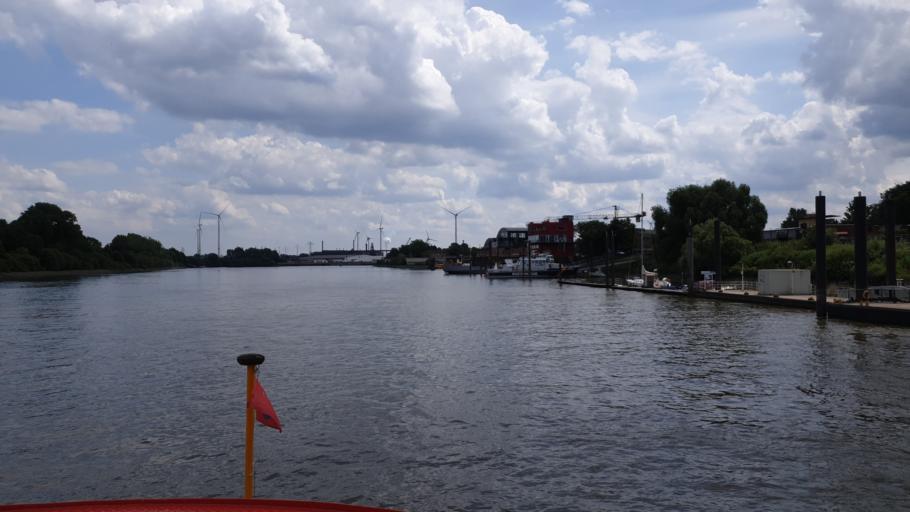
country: DE
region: Hamburg
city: Altona
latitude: 53.5369
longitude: 9.8790
